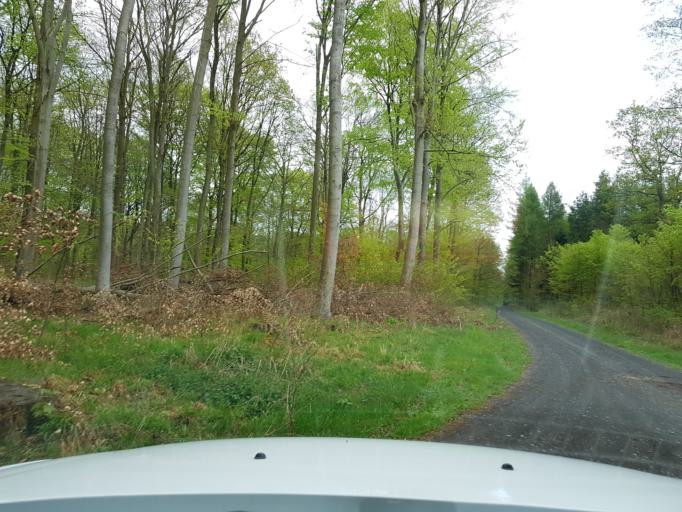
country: PL
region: West Pomeranian Voivodeship
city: Trzcinsko Zdroj
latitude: 52.9967
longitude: 14.6446
